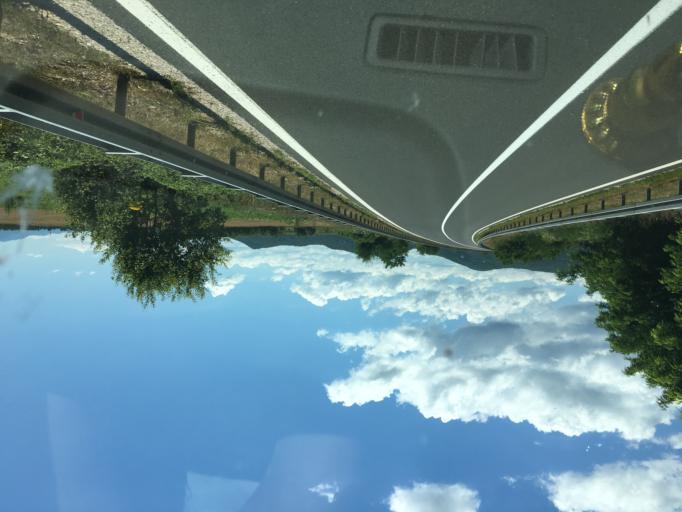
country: HR
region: Licko-Senjska
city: Gospic
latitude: 44.5752
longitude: 15.4072
